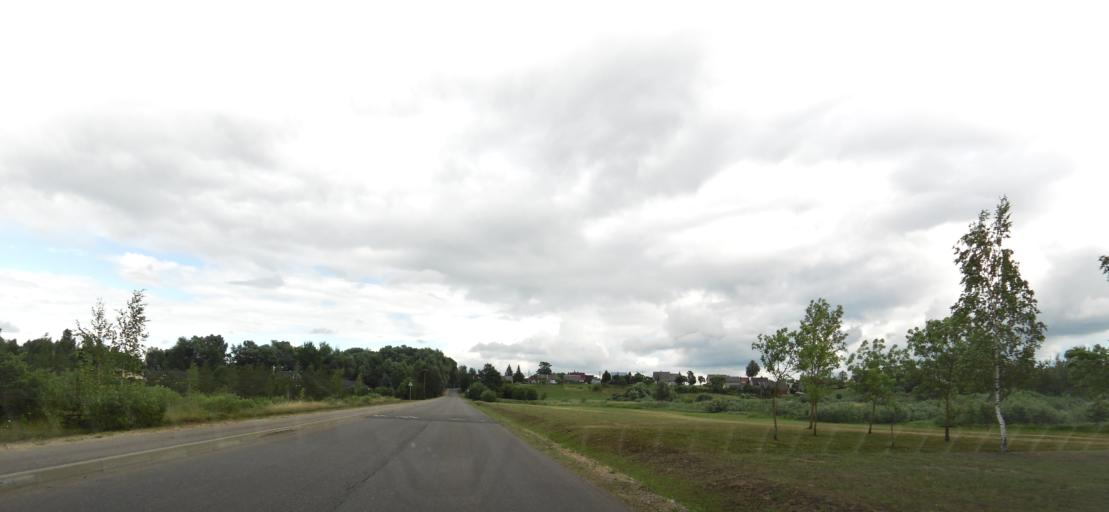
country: LT
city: Kupiskis
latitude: 55.8495
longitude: 24.9780
